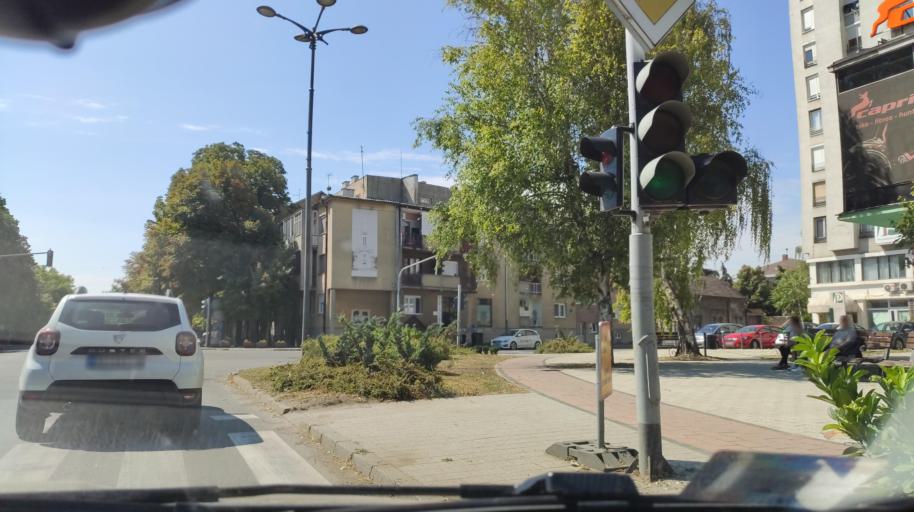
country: RS
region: Autonomna Pokrajina Vojvodina
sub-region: Severnobacki Okrug
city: Backa Topola
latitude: 45.8132
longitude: 19.6300
